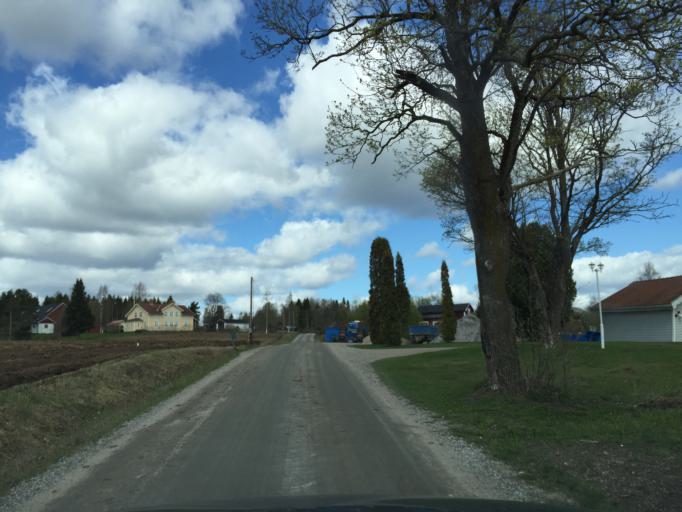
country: SE
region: Gaevleborg
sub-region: Bollnas Kommun
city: Arbra
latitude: 61.5171
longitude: 16.3518
